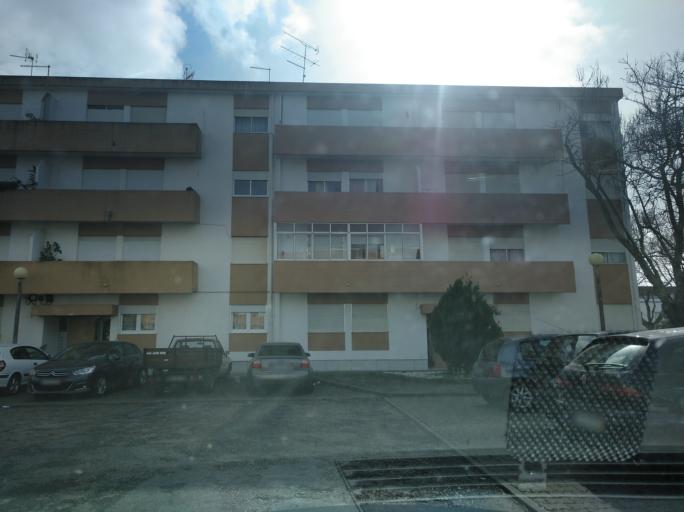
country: PT
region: Setubal
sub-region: Grandola
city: Grandola
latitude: 38.1744
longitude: -8.5617
